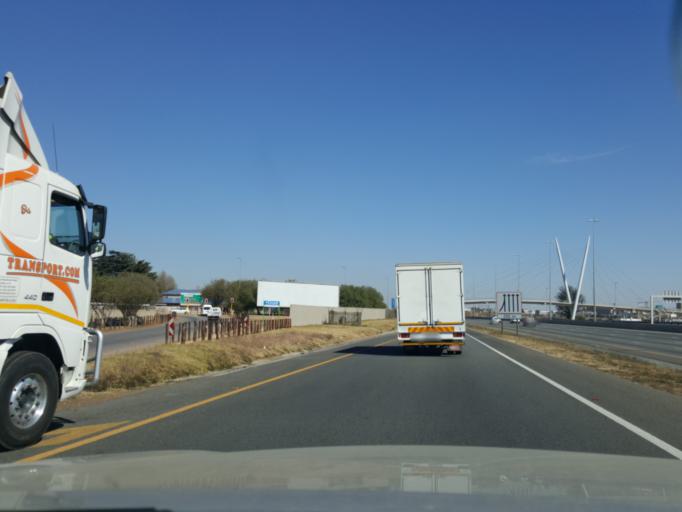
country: ZA
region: Gauteng
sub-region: City of Johannesburg Metropolitan Municipality
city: Modderfontein
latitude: -26.1347
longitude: 28.2248
